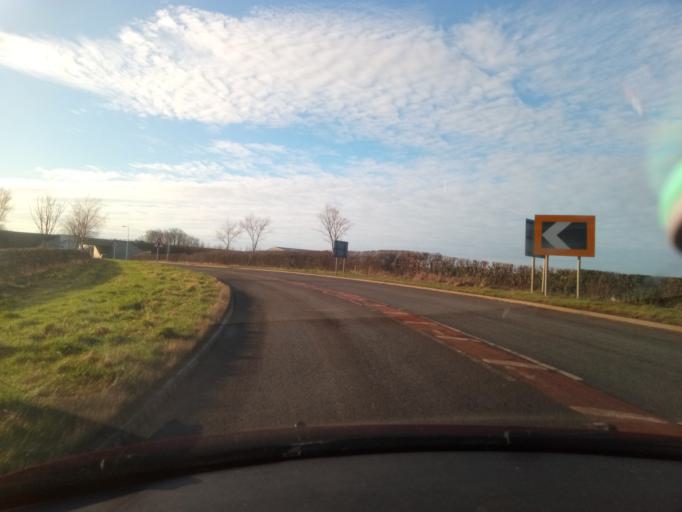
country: GB
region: England
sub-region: North Yorkshire
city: Ripon
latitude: 54.2247
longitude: -1.4843
